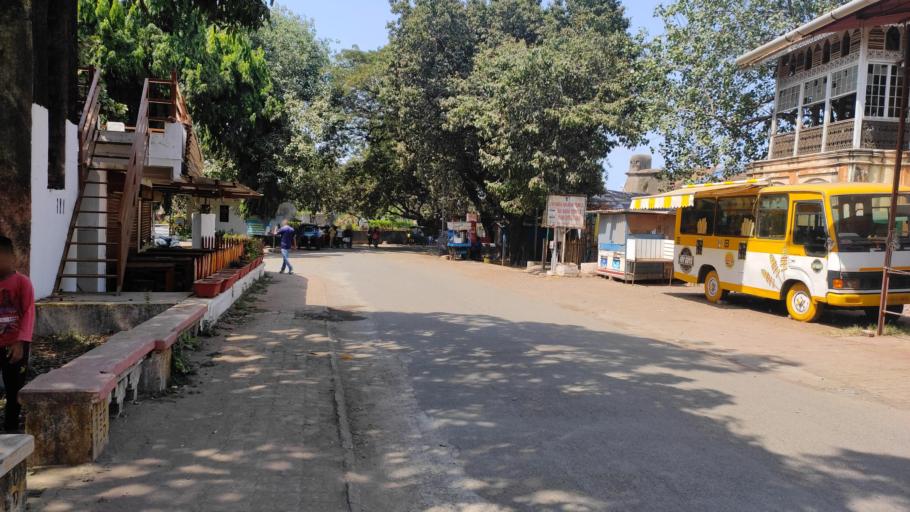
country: IN
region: Daman and Diu
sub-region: Daman District
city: Daman
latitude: 20.4139
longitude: 72.8335
